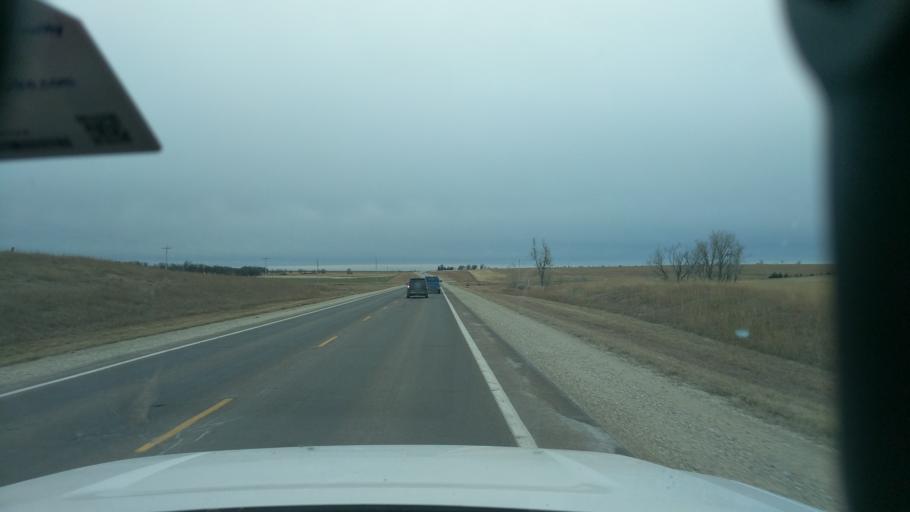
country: US
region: Kansas
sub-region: Dickinson County
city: Herington
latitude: 38.6125
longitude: -96.9486
